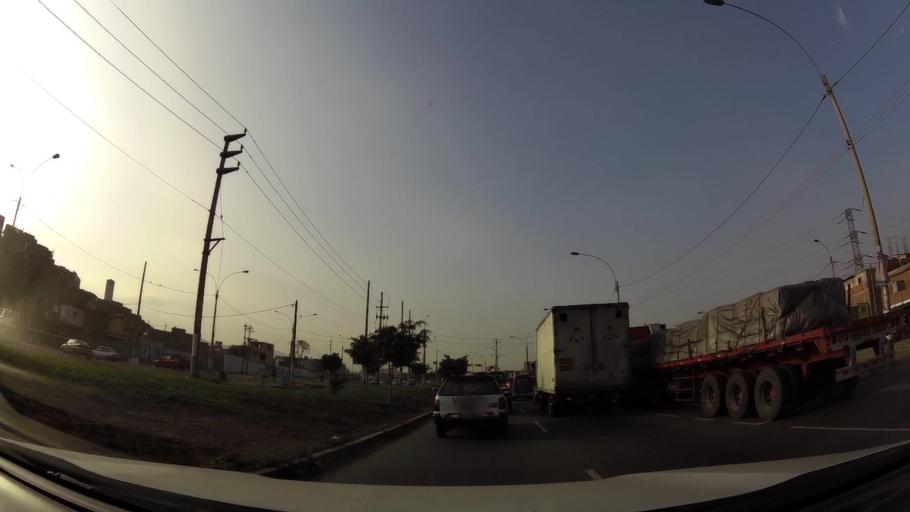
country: PE
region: Lima
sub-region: Lima
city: Independencia
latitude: -11.9690
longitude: -77.0840
